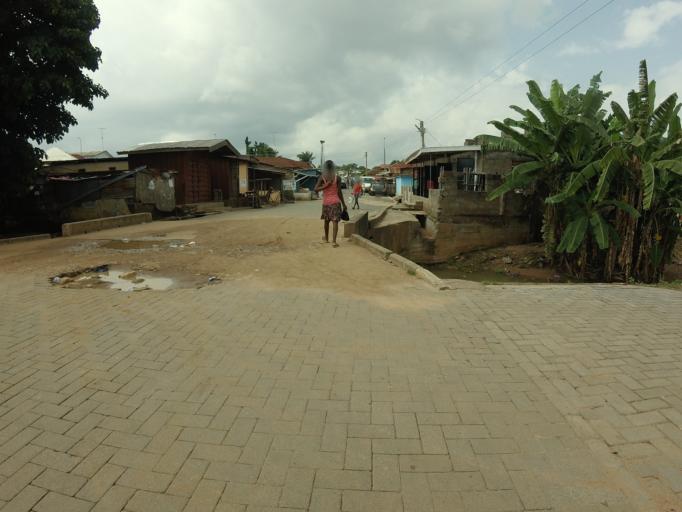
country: GH
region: Volta
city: Ho
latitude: 6.6149
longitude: 0.4698
